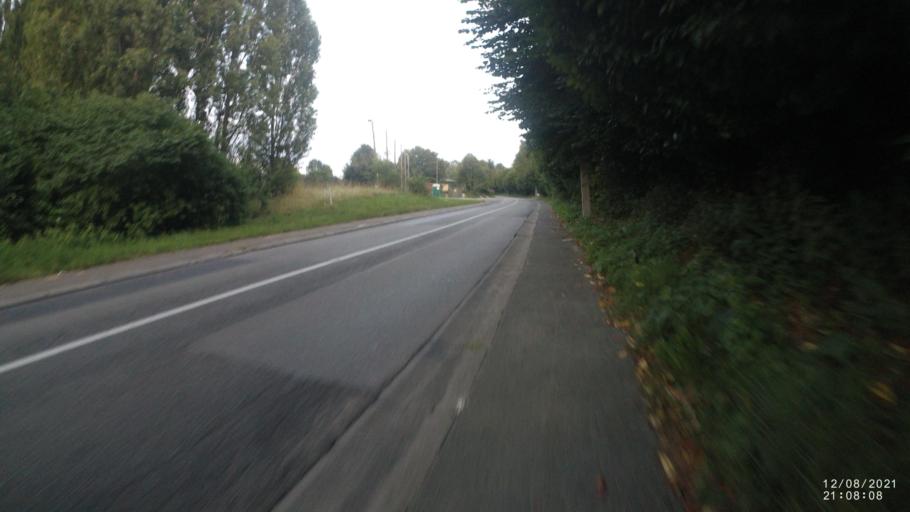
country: BE
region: Flanders
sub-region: Provincie Vlaams-Brabant
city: Dilbeek
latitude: 50.8496
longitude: 4.2523
